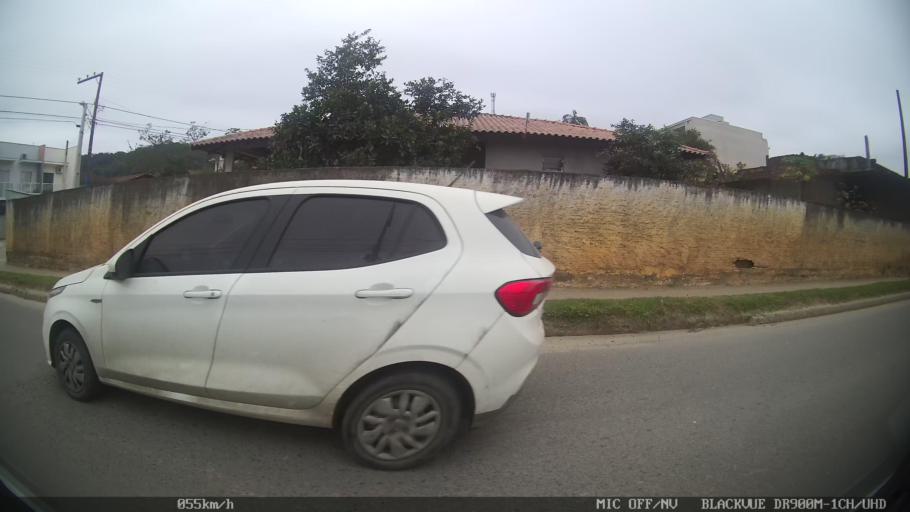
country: BR
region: Santa Catarina
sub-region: Joinville
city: Joinville
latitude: -26.3597
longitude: -48.8048
